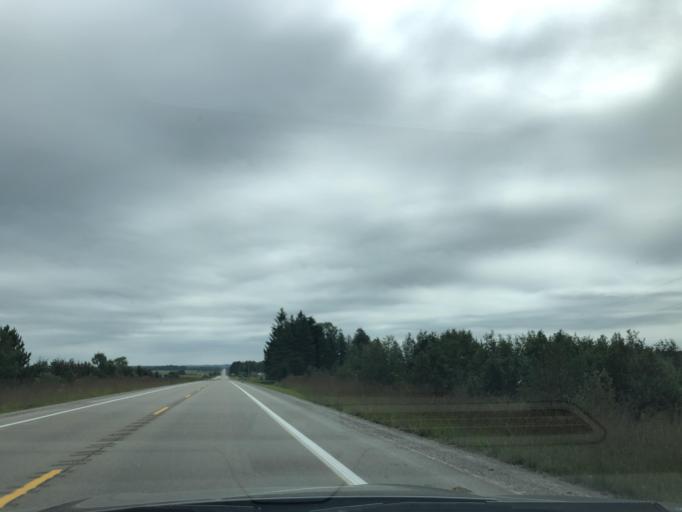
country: US
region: Michigan
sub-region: Clare County
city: Harrison
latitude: 44.0311
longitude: -84.9553
